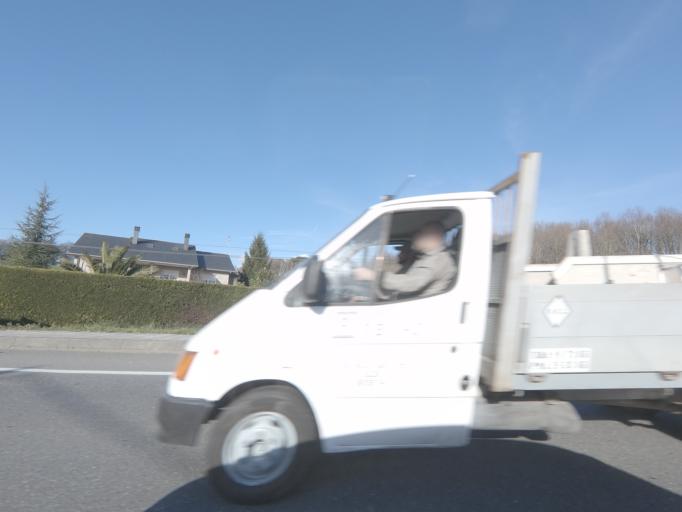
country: ES
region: Galicia
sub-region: Provincia de Pontevedra
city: Silleda
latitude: 42.7014
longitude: -8.2556
